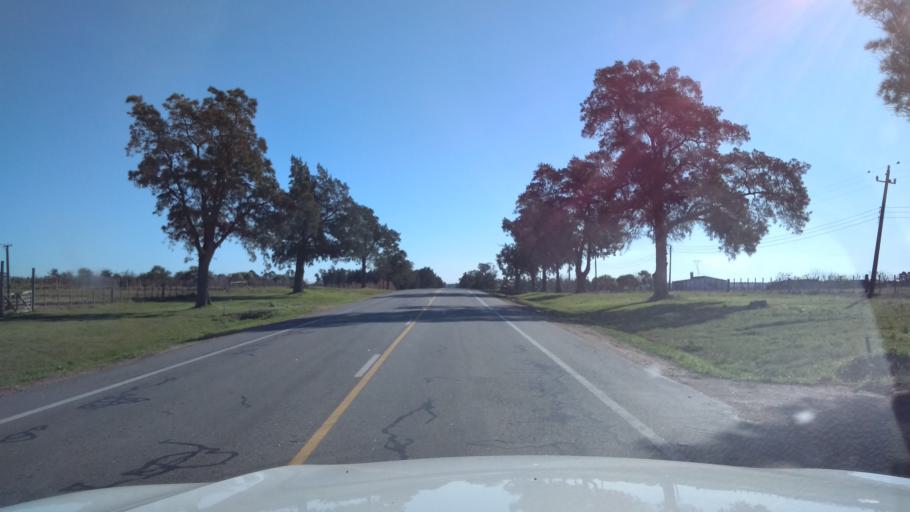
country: UY
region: Canelones
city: San Jacinto
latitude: -34.5394
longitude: -55.8995
